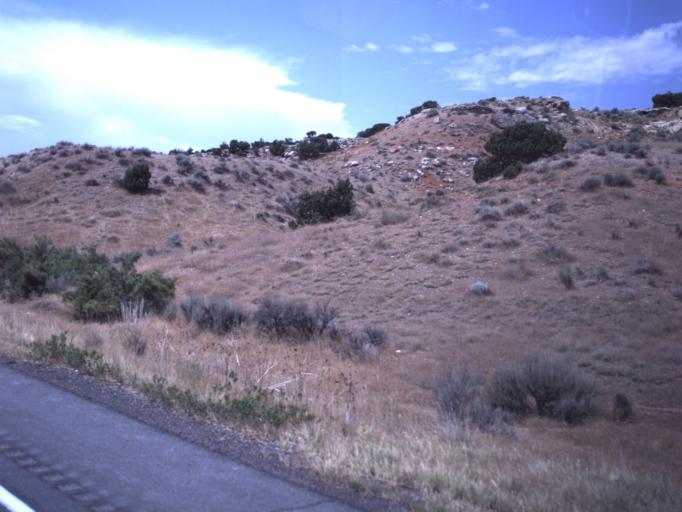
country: US
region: Utah
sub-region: Uintah County
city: Maeser
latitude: 40.3821
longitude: -109.6026
